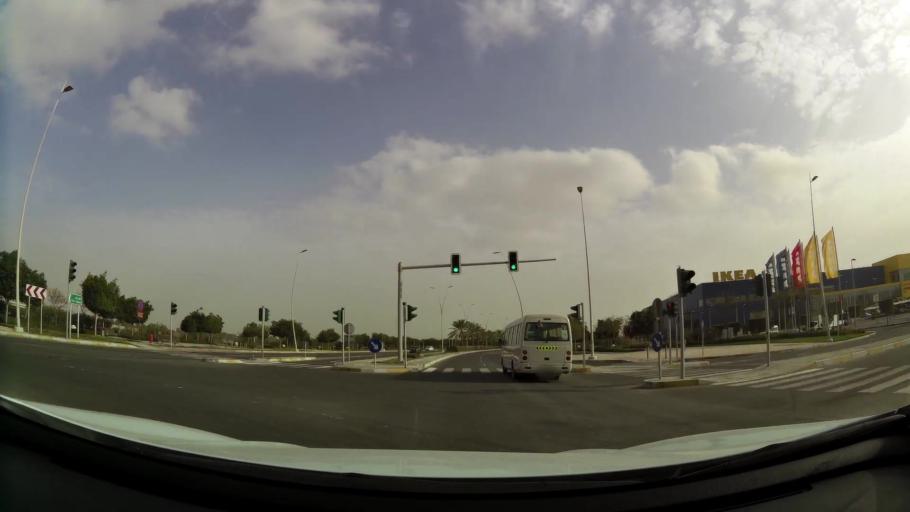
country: AE
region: Abu Dhabi
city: Abu Dhabi
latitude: 24.4915
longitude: 54.6142
